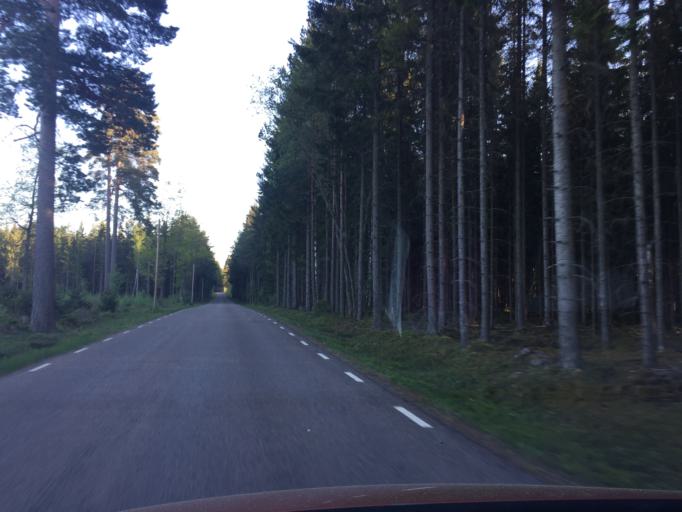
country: SE
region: Soedermanland
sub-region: Vingakers Kommun
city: Vingaker
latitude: 59.0081
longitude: 15.6758
